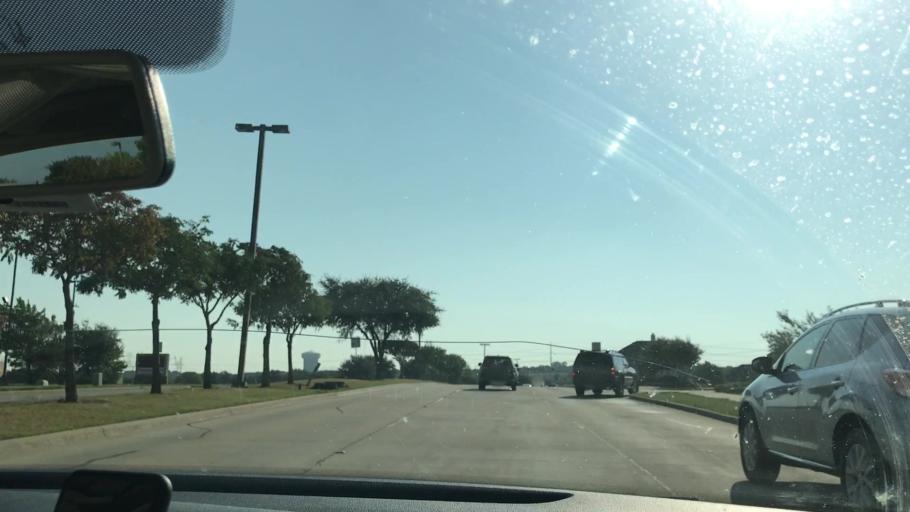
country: US
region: Texas
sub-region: Denton County
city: Lewisville
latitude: 33.0202
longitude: -96.9286
